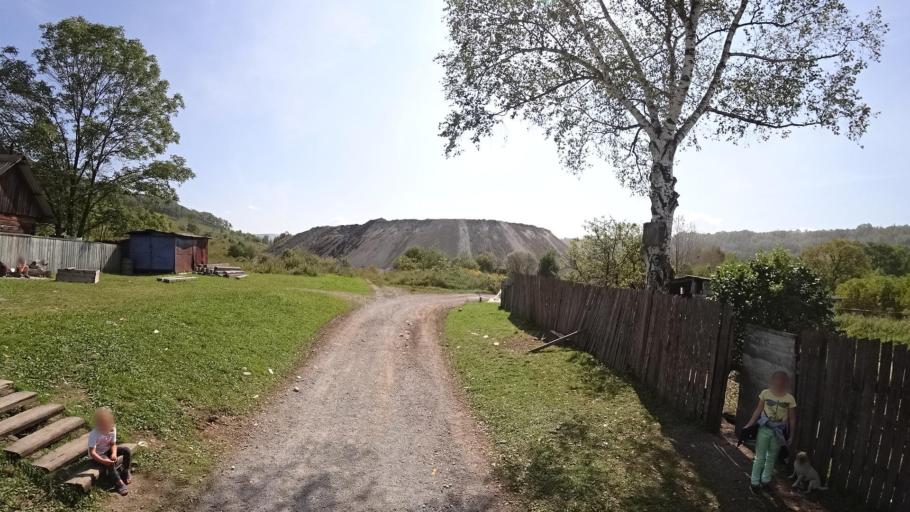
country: RU
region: Jewish Autonomous Oblast
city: Londoko
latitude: 49.0218
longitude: 131.9337
